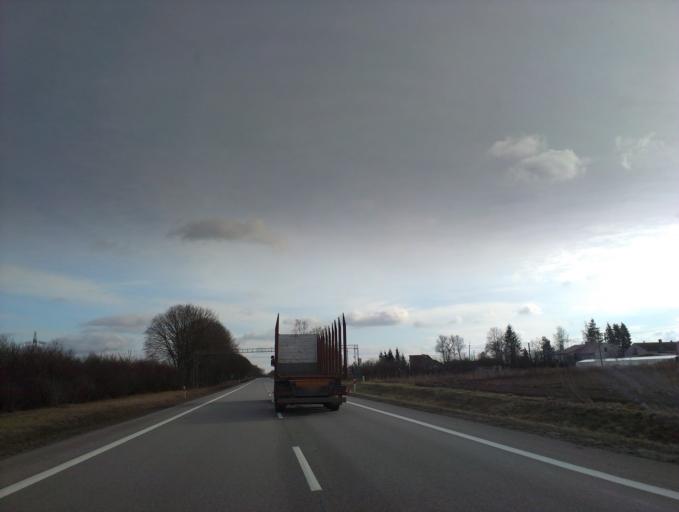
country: PL
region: Kujawsko-Pomorskie
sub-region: Powiat lipnowski
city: Kikol
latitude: 52.8819
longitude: 19.1386
